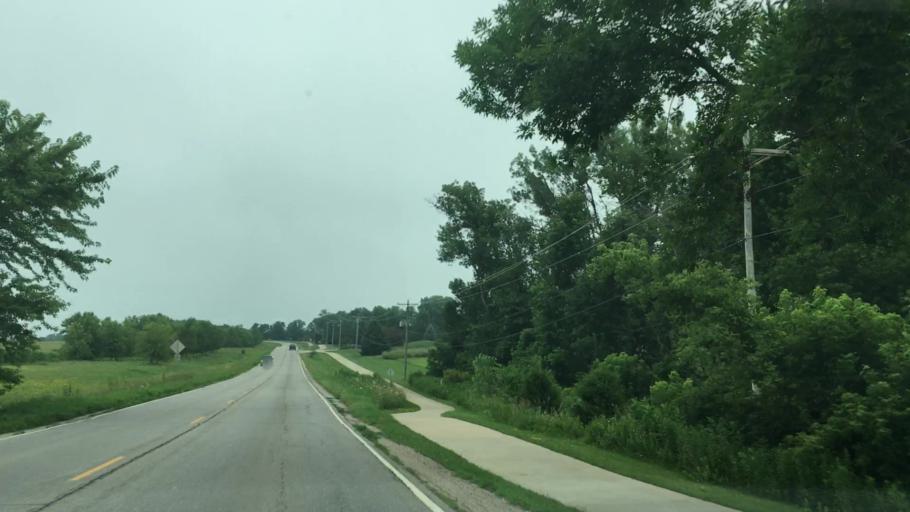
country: US
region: Iowa
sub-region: Johnson County
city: North Liberty
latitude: 41.7244
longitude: -91.5610
